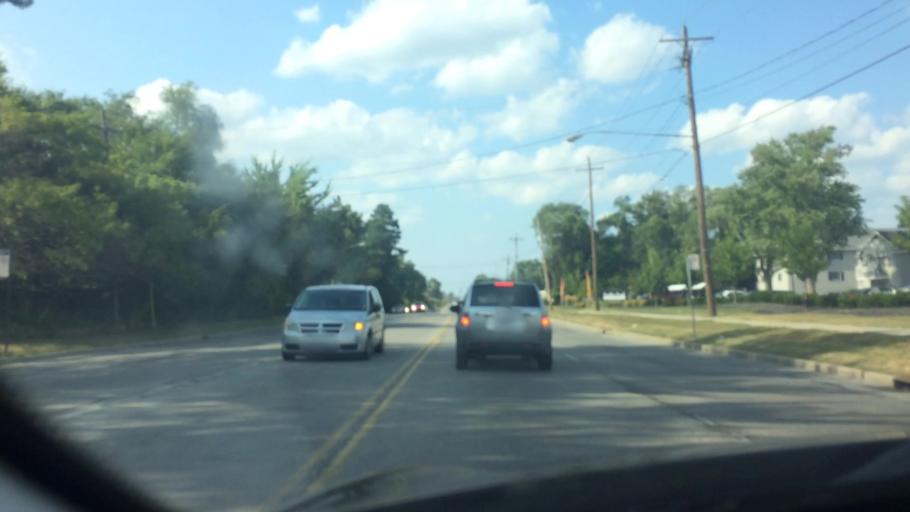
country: US
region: Ohio
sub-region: Lucas County
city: Ottawa Hills
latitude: 41.6161
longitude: -83.6257
